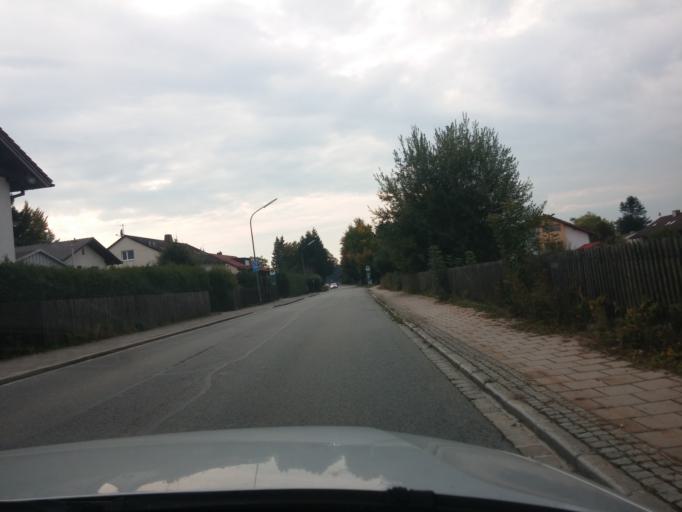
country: DE
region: Bavaria
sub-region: Upper Bavaria
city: Sauerlach
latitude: 47.9704
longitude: 11.6430
